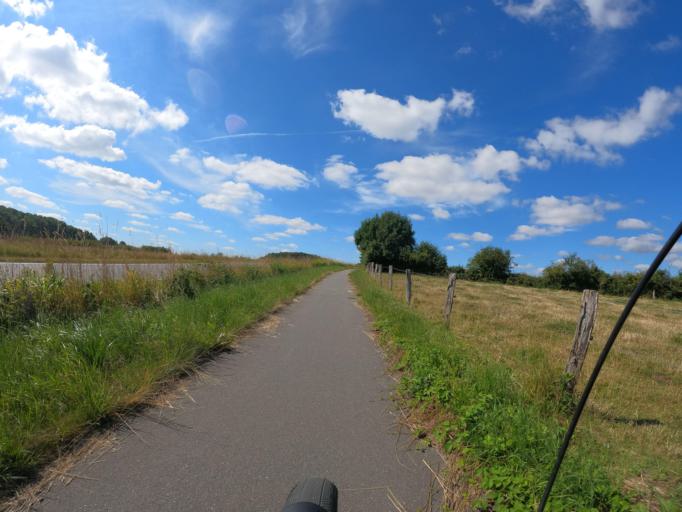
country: DE
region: Schleswig-Holstein
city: Dollerup
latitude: 54.7895
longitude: 9.7106
